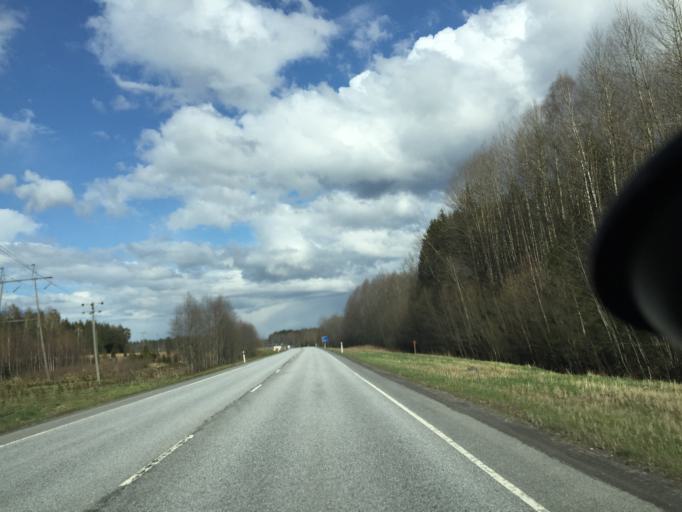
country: FI
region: Uusimaa
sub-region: Raaseporin
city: Karis
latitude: 60.0420
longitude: 23.6215
